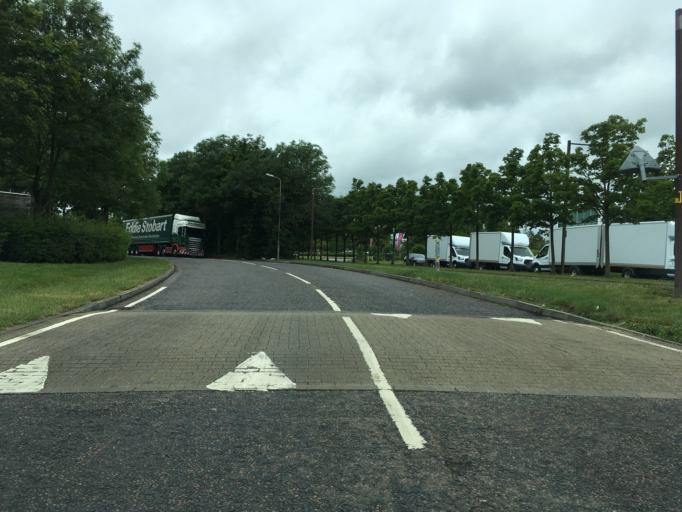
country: GB
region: England
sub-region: Milton Keynes
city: Broughton
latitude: 52.0374
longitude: -0.6869
